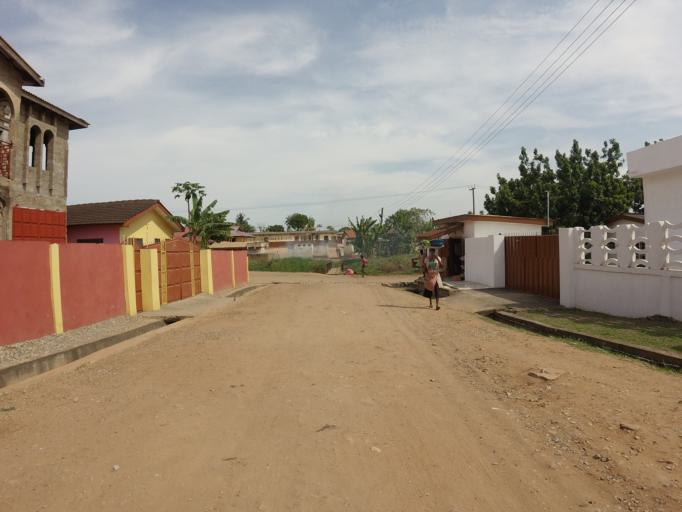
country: GH
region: Greater Accra
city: Dome
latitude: 5.6267
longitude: -0.2319
